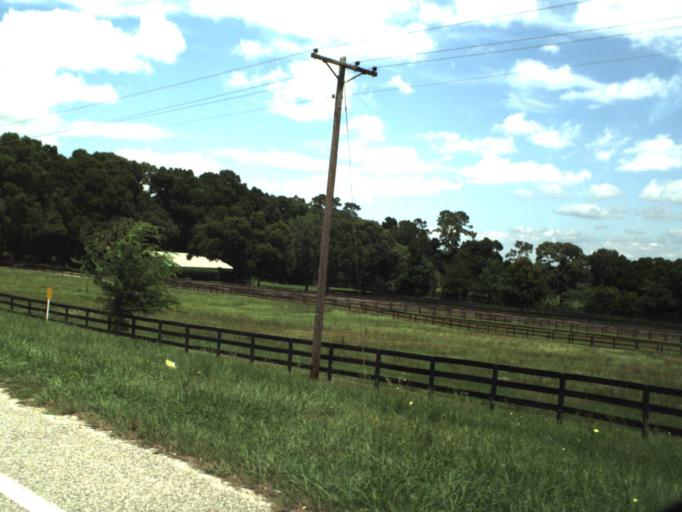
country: US
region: Florida
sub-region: Marion County
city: Citra
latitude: 29.3967
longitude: -82.1978
